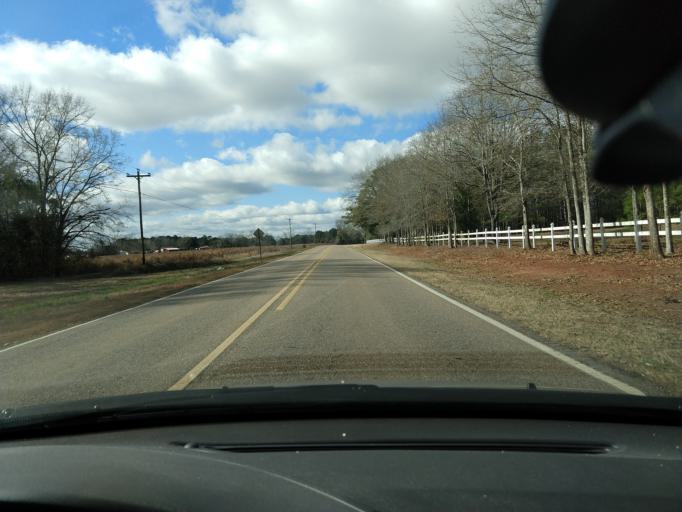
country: US
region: Alabama
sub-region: Coffee County
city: Enterprise
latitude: 31.3208
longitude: -85.9053
